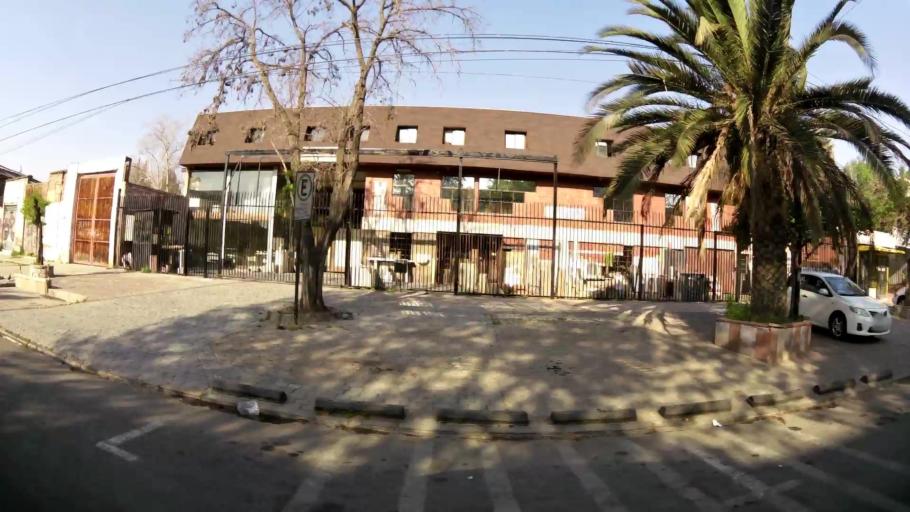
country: CL
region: Santiago Metropolitan
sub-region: Provincia de Santiago
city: Santiago
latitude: -33.4190
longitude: -70.6503
